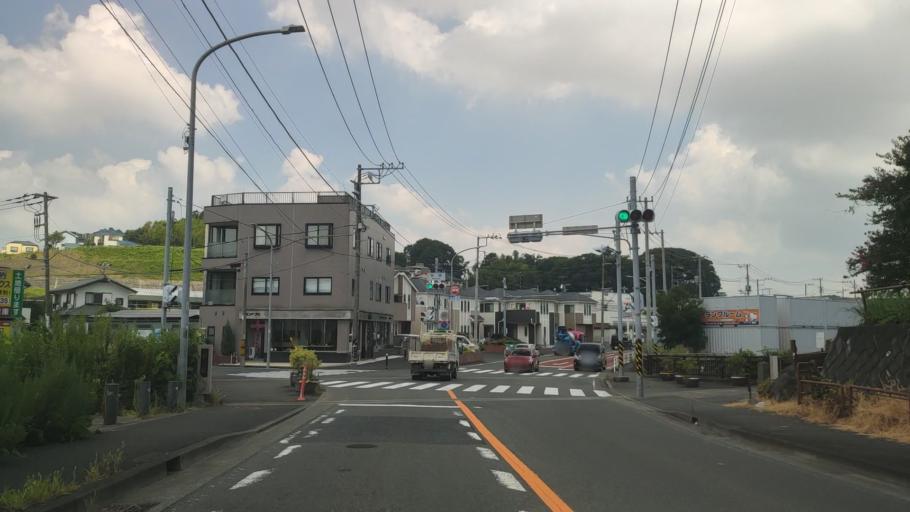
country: JP
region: Kanagawa
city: Minami-rinkan
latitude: 35.4320
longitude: 139.5128
